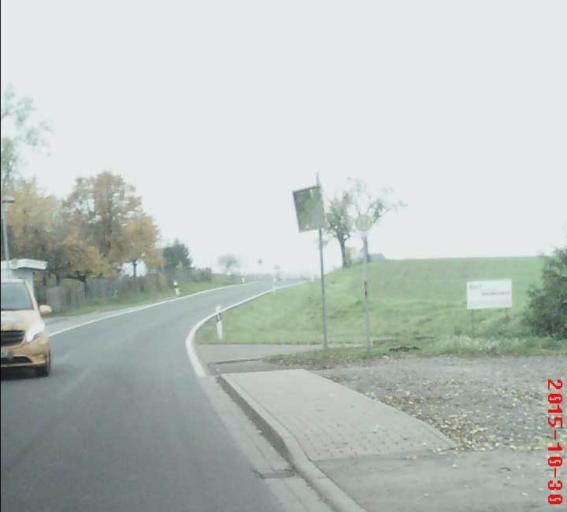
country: DE
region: Thuringia
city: Anrode
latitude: 51.2398
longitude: 10.3742
